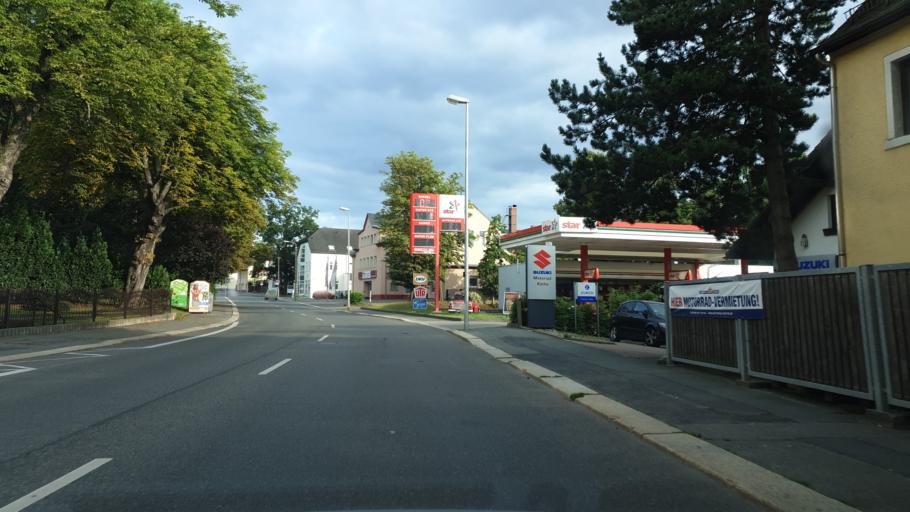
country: DE
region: Saxony
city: Hilbersdorf
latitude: 50.8311
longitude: 12.9576
